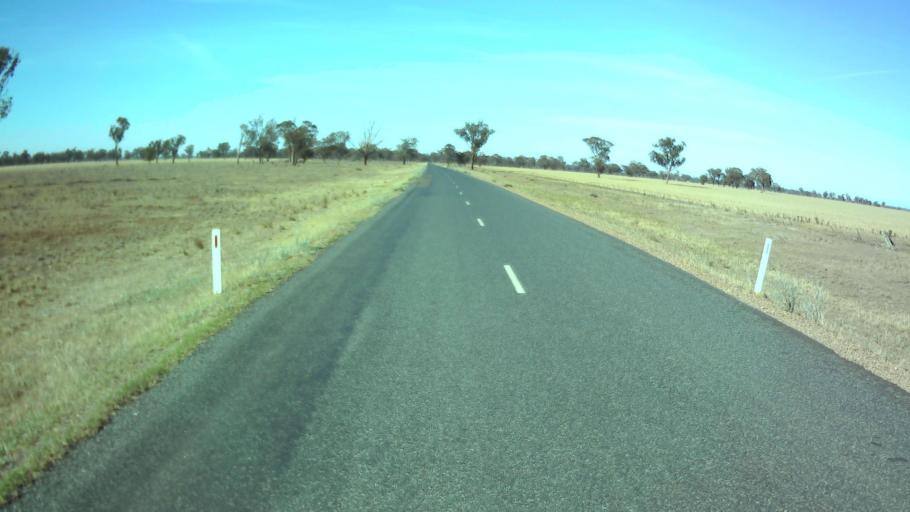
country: AU
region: New South Wales
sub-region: Weddin
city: Grenfell
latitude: -34.0509
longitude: 147.9193
